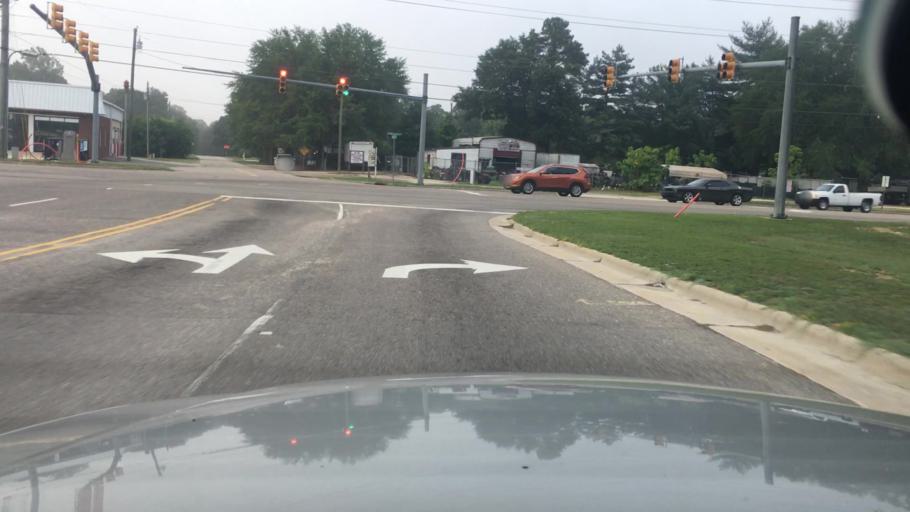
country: US
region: North Carolina
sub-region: Cumberland County
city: Hope Mills
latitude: 35.0146
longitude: -78.9355
